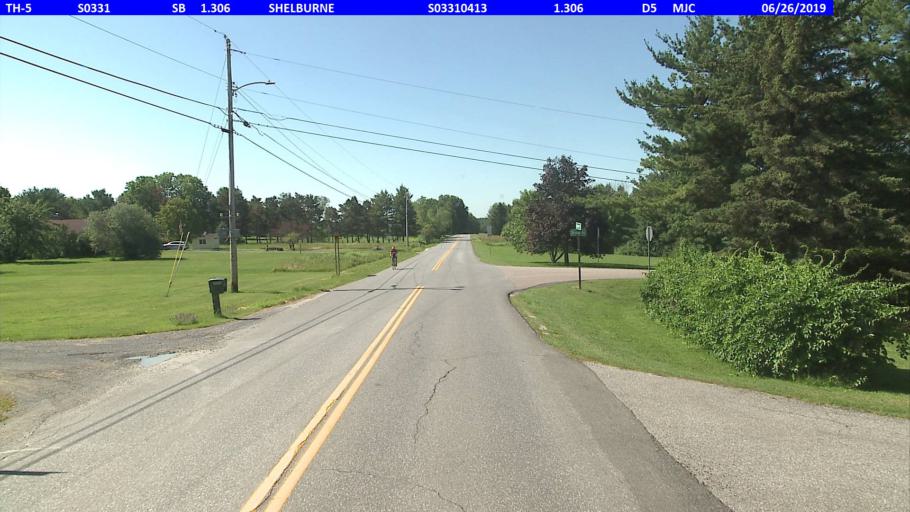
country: US
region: Vermont
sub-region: Chittenden County
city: South Burlington
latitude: 44.3896
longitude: -73.1760
